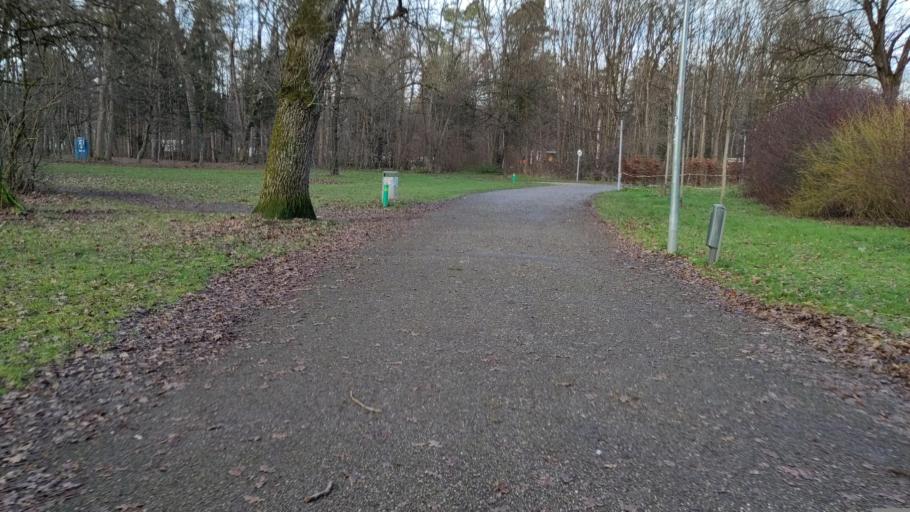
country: DE
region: Bavaria
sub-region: Upper Bavaria
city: Pullach im Isartal
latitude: 48.1034
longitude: 11.5185
